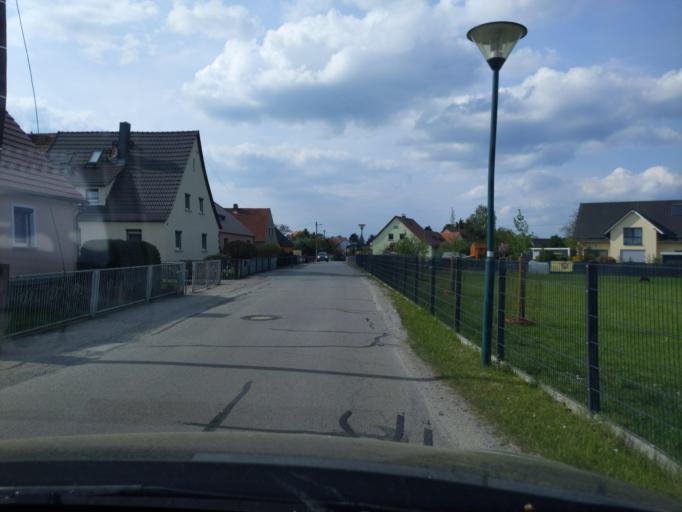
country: DE
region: Saxony
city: Malschwitz
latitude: 51.2356
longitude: 14.5248
